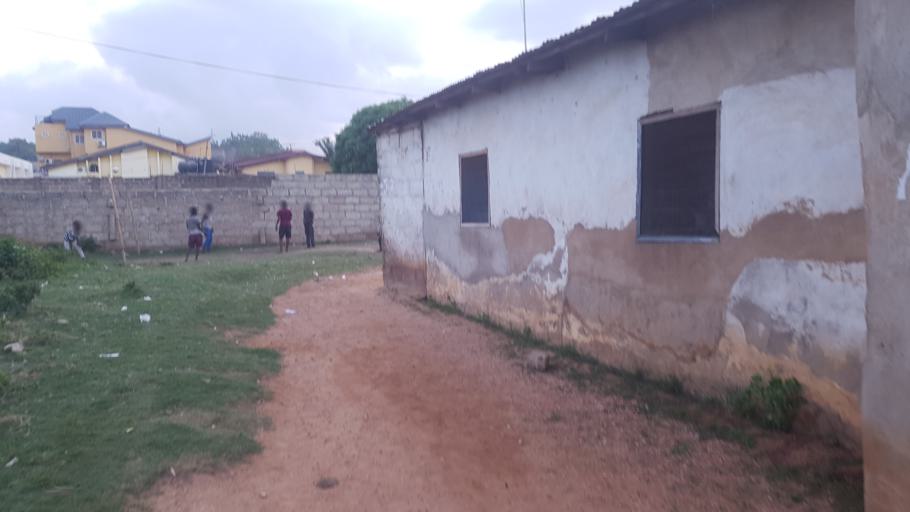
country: GH
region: Greater Accra
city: Gbawe
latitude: 5.5529
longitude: -0.3497
